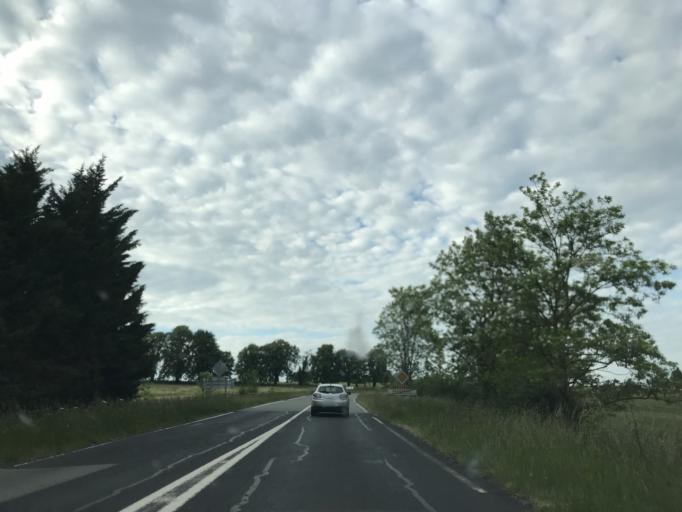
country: FR
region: Auvergne
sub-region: Departement du Puy-de-Dome
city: Randan
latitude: 46.0460
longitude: 3.3621
